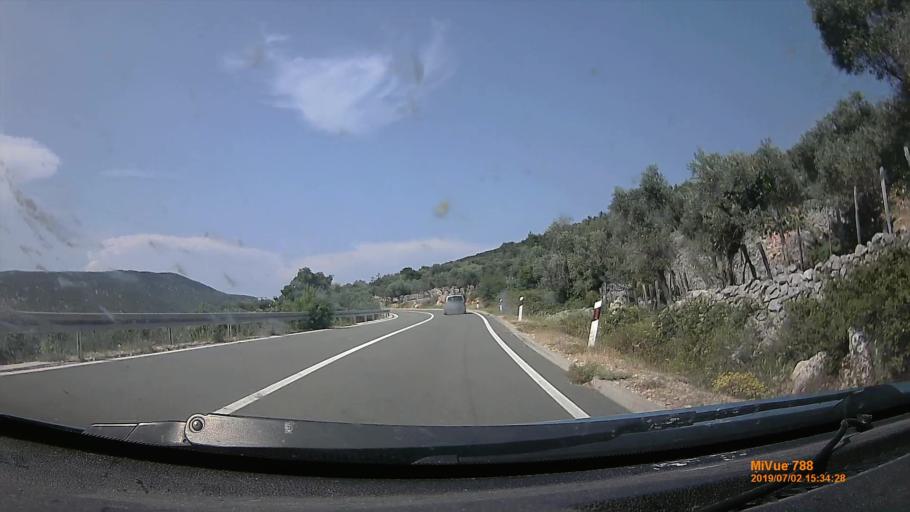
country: HR
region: Primorsko-Goranska
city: Cres
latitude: 44.9674
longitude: 14.4127
